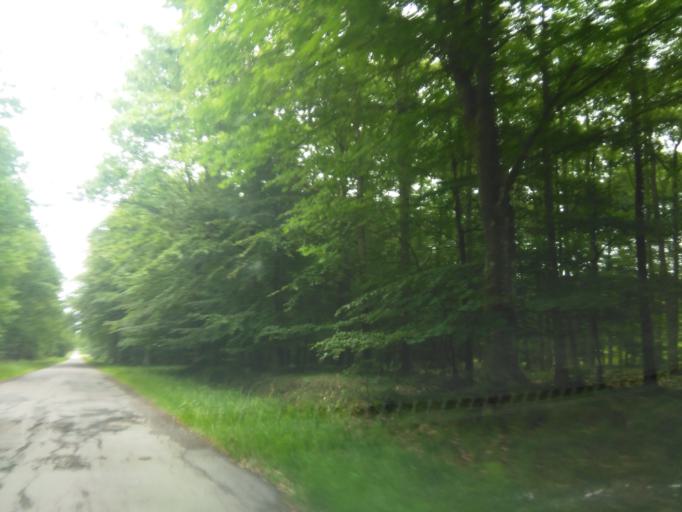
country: DK
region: Capital Region
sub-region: Bornholm Kommune
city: Akirkeby
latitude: 55.1119
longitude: 14.9360
